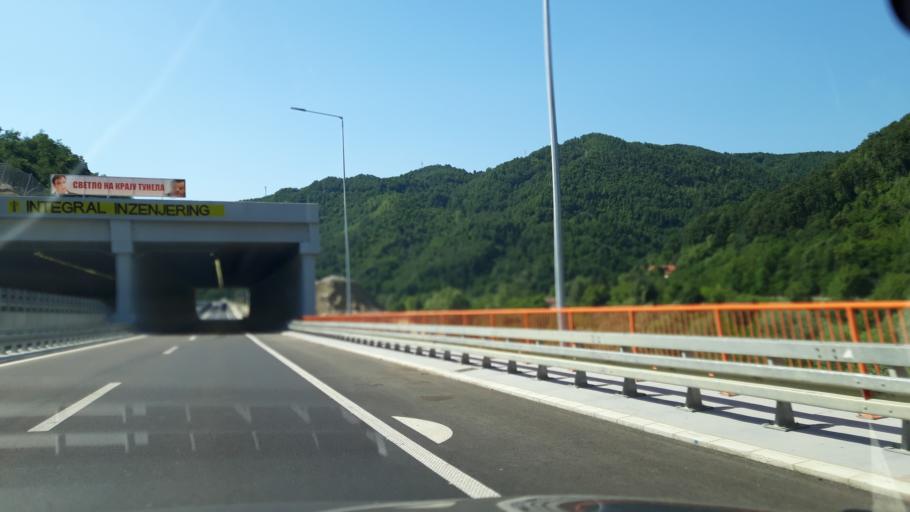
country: RS
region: Central Serbia
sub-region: Jablanicki Okrug
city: Vlasotince
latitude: 42.8674
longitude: 22.1065
